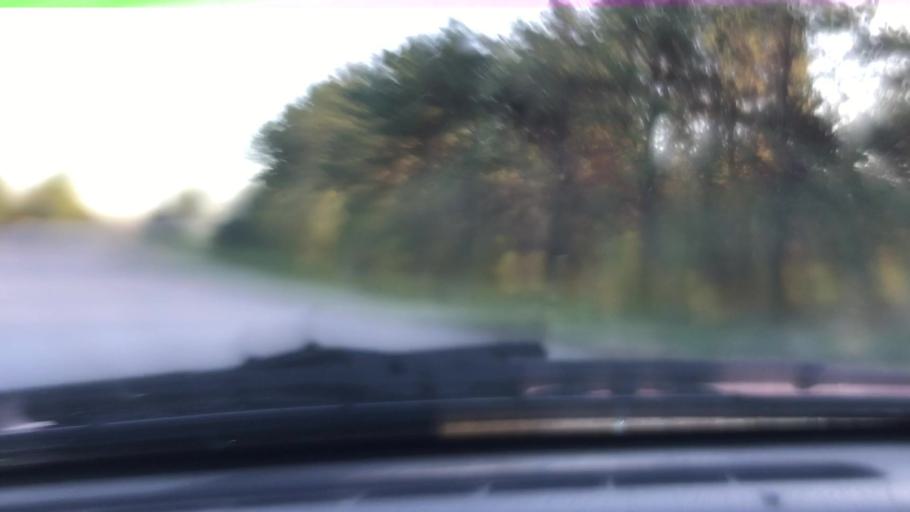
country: US
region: Nebraska
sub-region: Lancaster County
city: Lincoln
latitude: 40.7527
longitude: -96.7538
